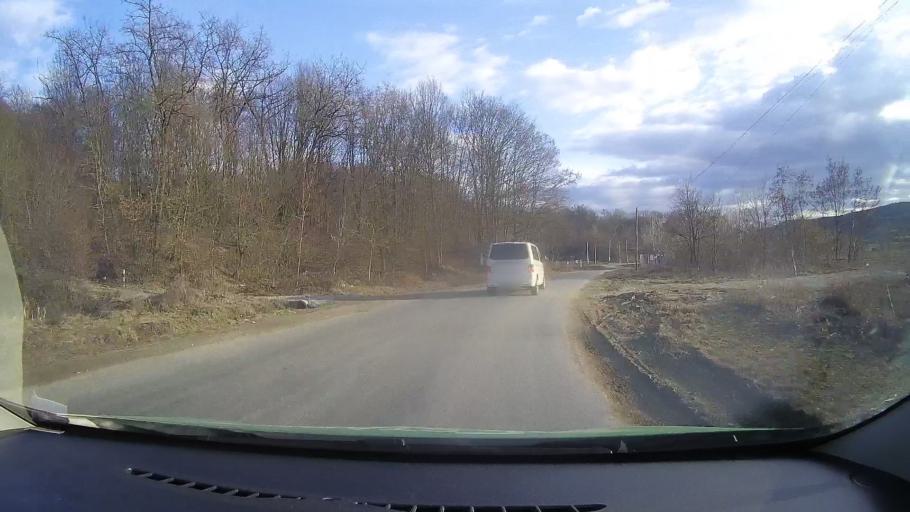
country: RO
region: Dambovita
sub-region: Comuna Ocnita
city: Ocnita
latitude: 44.9687
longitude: 25.5481
